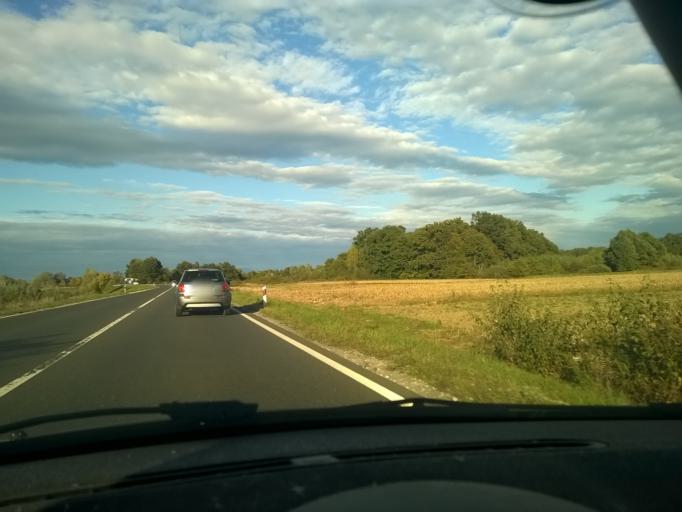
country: HR
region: Zagrebacka
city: Pojatno
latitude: 45.9215
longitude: 15.8215
